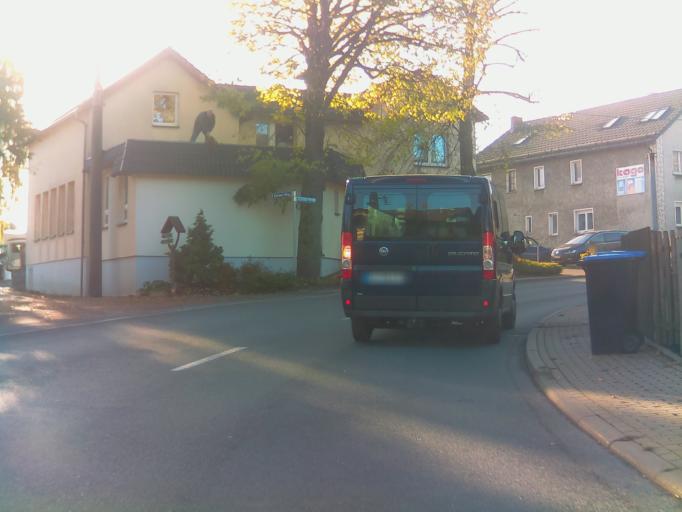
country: DE
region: Thuringia
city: Saalfeld
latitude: 50.6088
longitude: 11.3166
